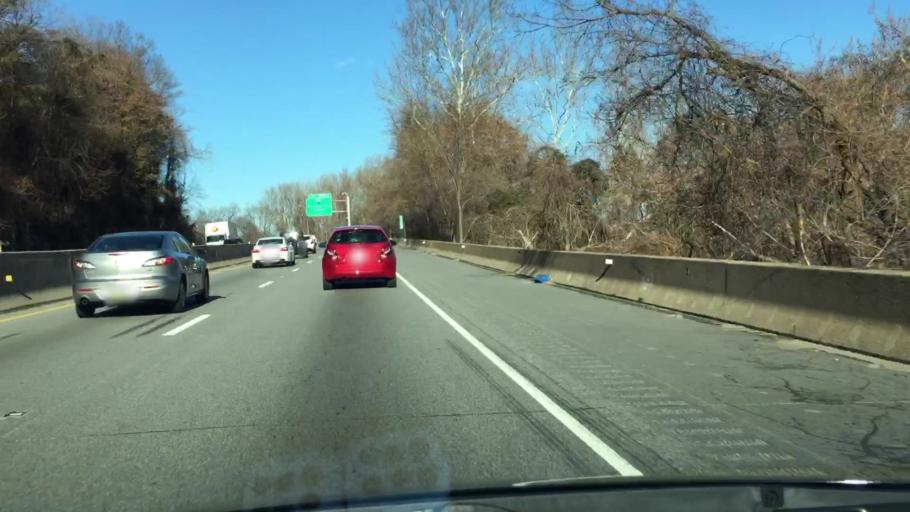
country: US
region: Pennsylvania
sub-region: Montgomery County
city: Conshohocken
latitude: 40.0680
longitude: -75.2787
